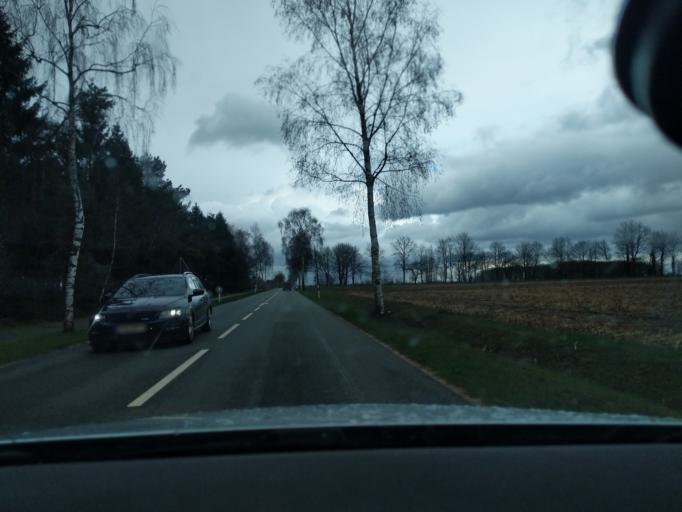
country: DE
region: Lower Saxony
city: Kutenholz
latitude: 53.5053
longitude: 9.3573
